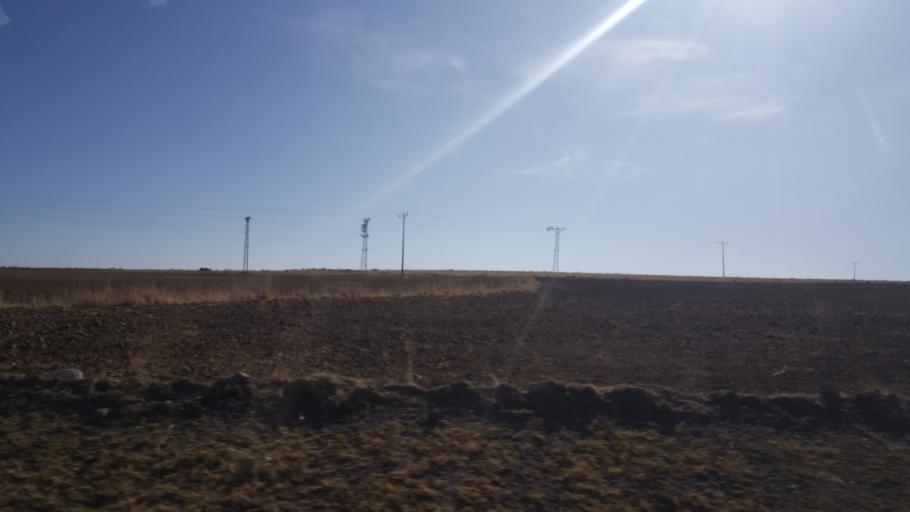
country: TR
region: Ankara
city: Altpinar
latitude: 39.2406
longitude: 32.7366
